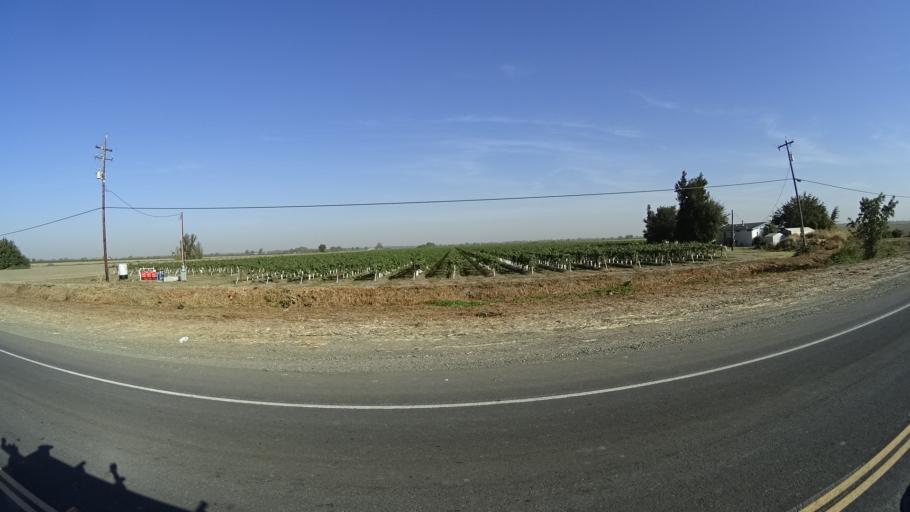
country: US
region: California
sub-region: Sacramento County
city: Parkway
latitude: 38.4147
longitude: -121.5654
